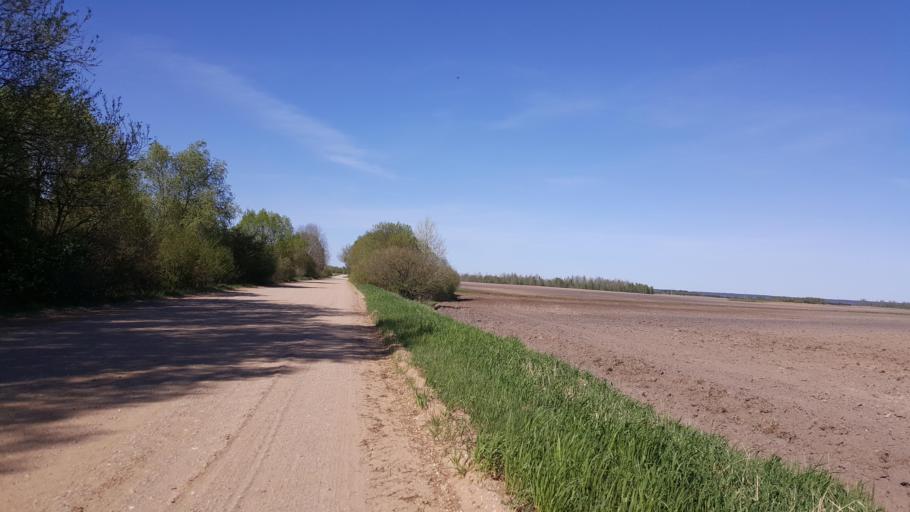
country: BY
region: Brest
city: Kamyanyets
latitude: 52.4268
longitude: 23.8807
